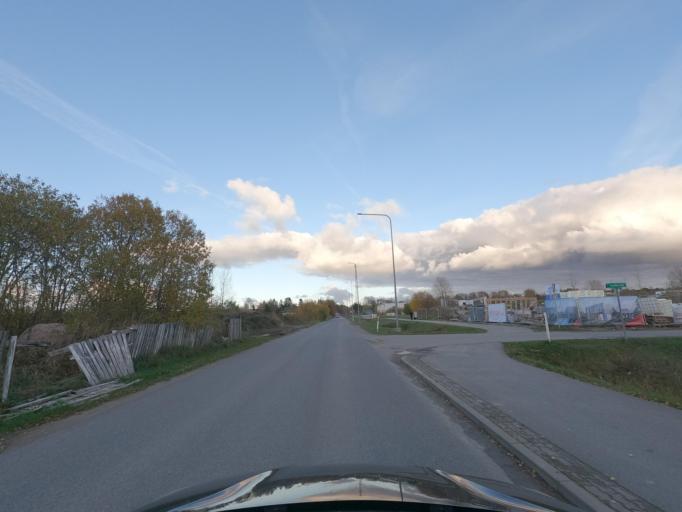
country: EE
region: Harju
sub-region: Saue vald
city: Laagri
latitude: 59.3641
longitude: 24.5858
